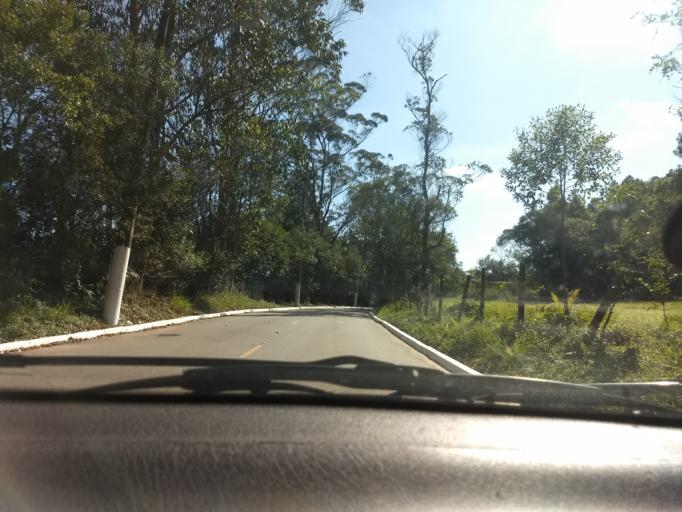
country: BR
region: Sao Paulo
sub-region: Embu-Guacu
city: Embu Guacu
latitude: -23.8104
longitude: -46.7622
